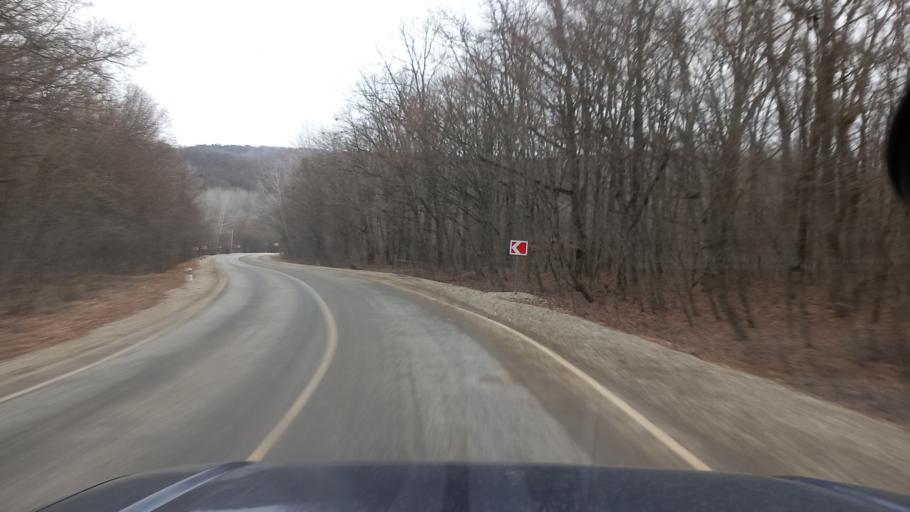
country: RU
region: Krasnodarskiy
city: Saratovskaya
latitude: 44.5434
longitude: 39.2912
